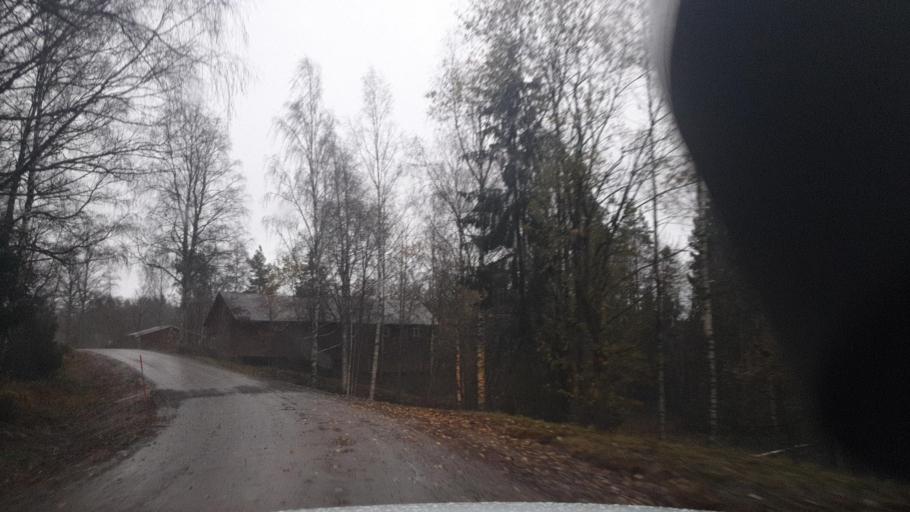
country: NO
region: Hedmark
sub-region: Eidskog
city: Skotterud
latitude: 59.7379
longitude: 12.0785
